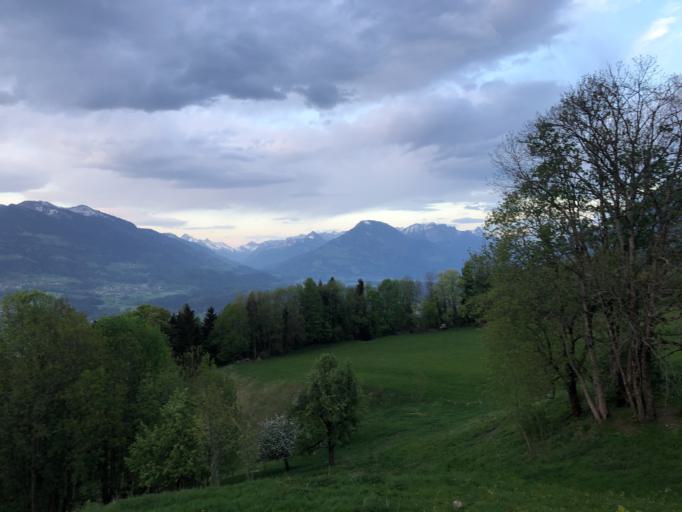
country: AT
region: Vorarlberg
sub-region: Politischer Bezirk Feldkirch
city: Satteins
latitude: 47.1896
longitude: 9.6469
